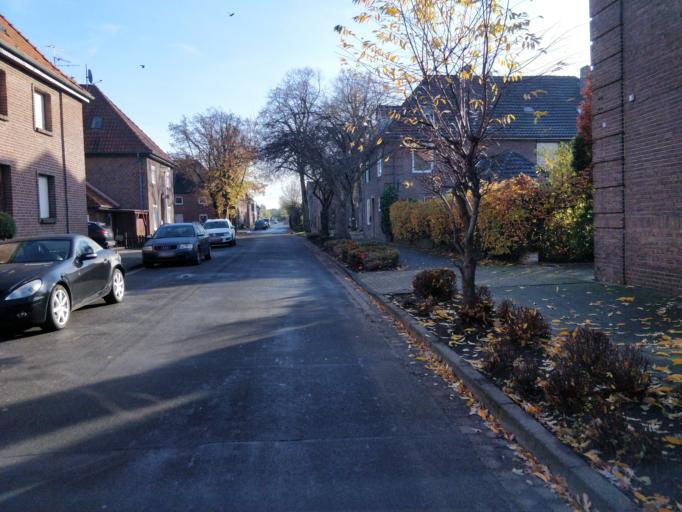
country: DE
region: North Rhine-Westphalia
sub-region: Regierungsbezirk Dusseldorf
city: Emmerich
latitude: 51.8490
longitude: 6.2428
